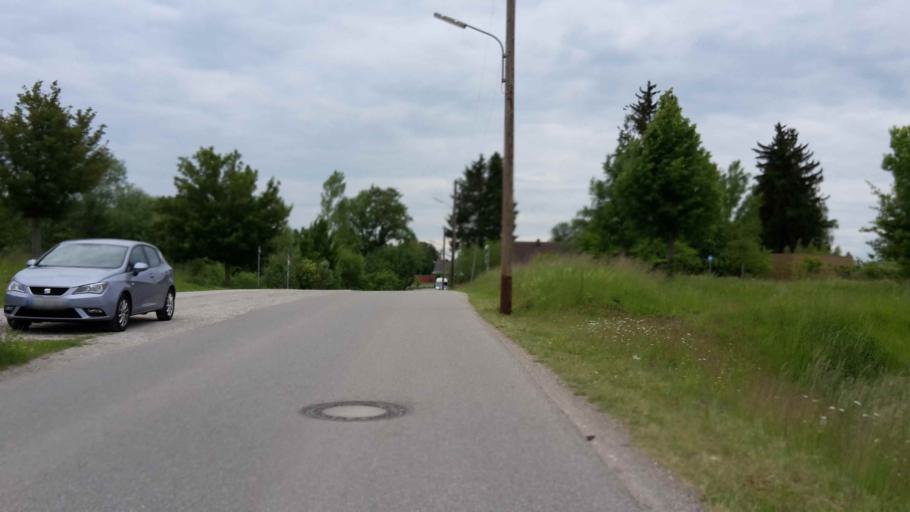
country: DE
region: Bavaria
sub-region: Upper Bavaria
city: Pasing
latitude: 48.1680
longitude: 11.4152
